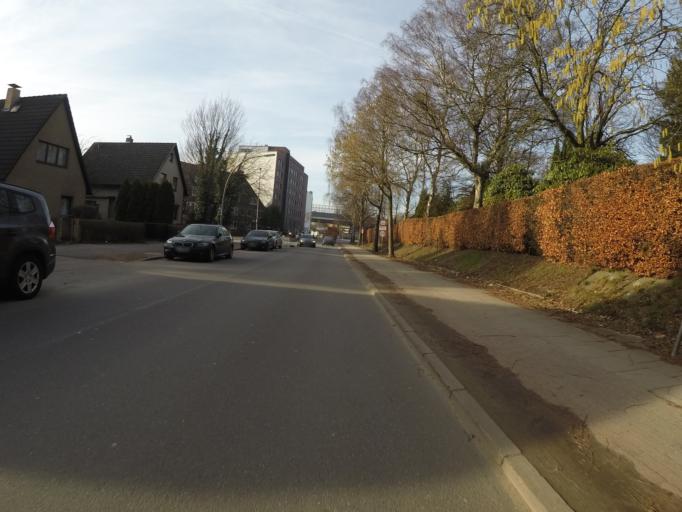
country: DE
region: Hamburg
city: Stellingen
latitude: 53.5894
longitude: 9.9211
